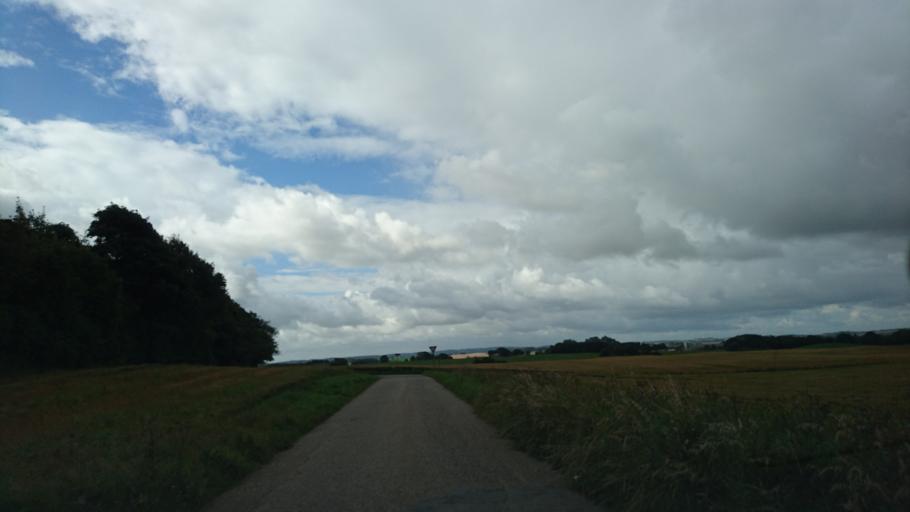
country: DK
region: North Denmark
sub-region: Hjorring Kommune
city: Sindal
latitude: 57.3789
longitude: 10.2434
